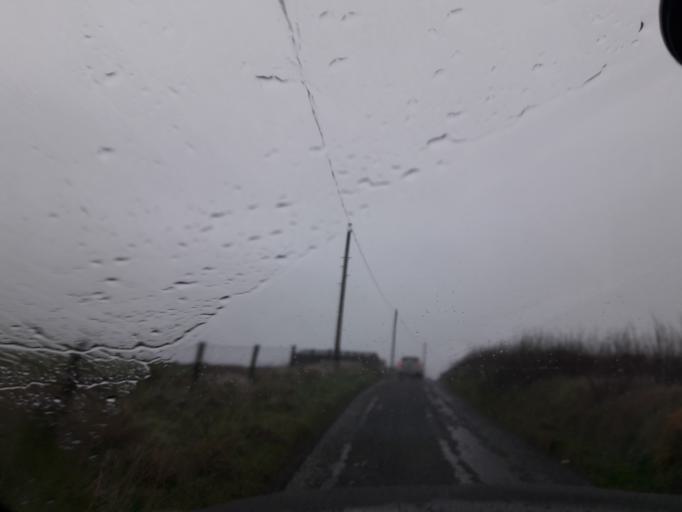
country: IE
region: Ulster
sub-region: County Donegal
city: Ramelton
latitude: 55.2664
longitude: -7.6466
